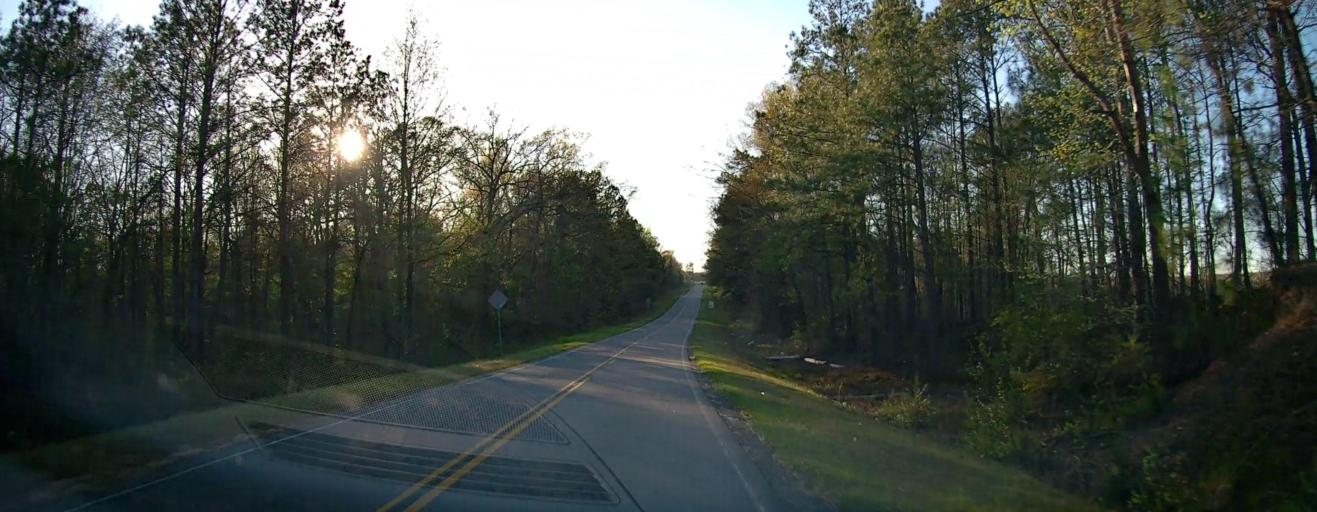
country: US
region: Georgia
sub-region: Wilkinson County
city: Gordon
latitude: 32.8782
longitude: -83.2715
